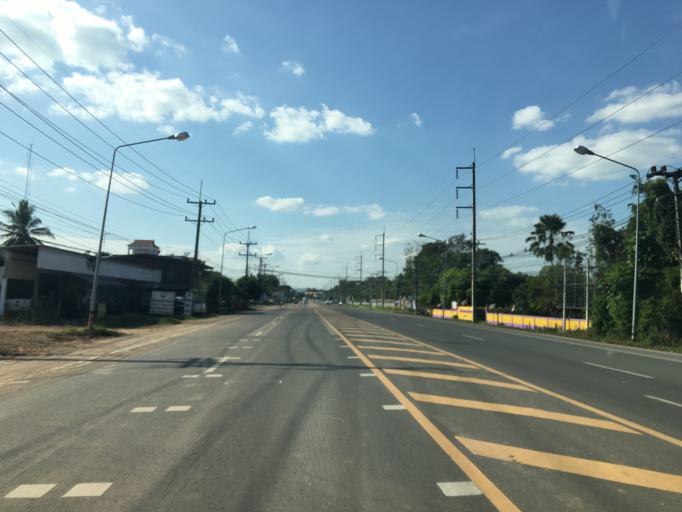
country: TH
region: Phayao
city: Chun
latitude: 19.3350
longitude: 100.1359
